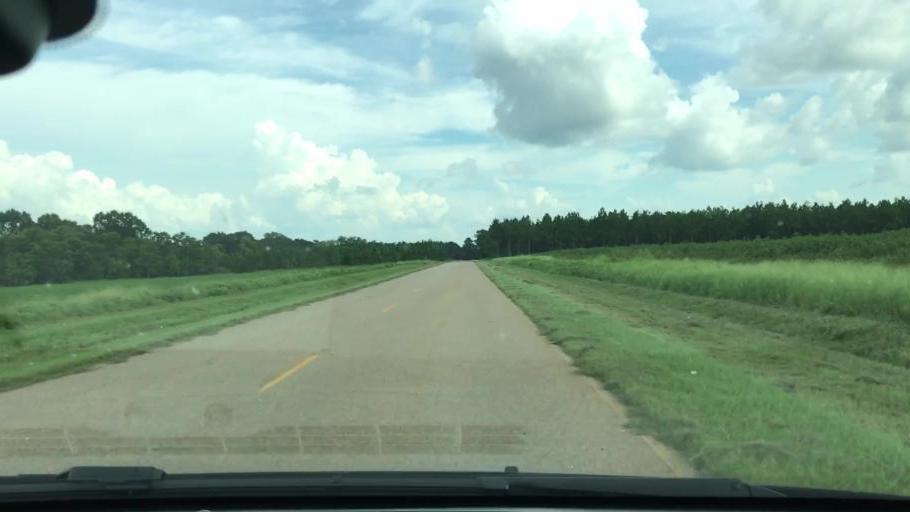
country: US
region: Georgia
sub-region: Clay County
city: Fort Gaines
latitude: 31.5634
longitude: -84.9852
